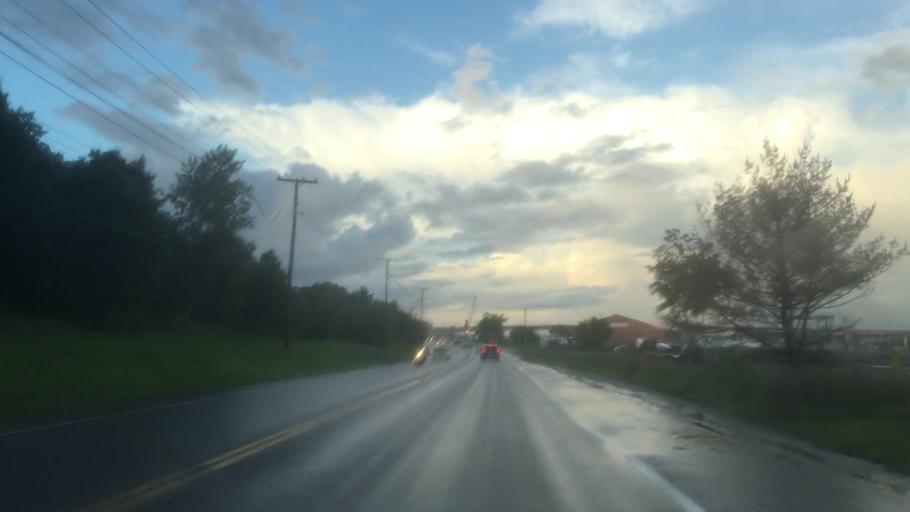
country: US
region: Maine
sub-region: Cumberland County
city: Portland
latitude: 43.6436
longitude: -70.2705
